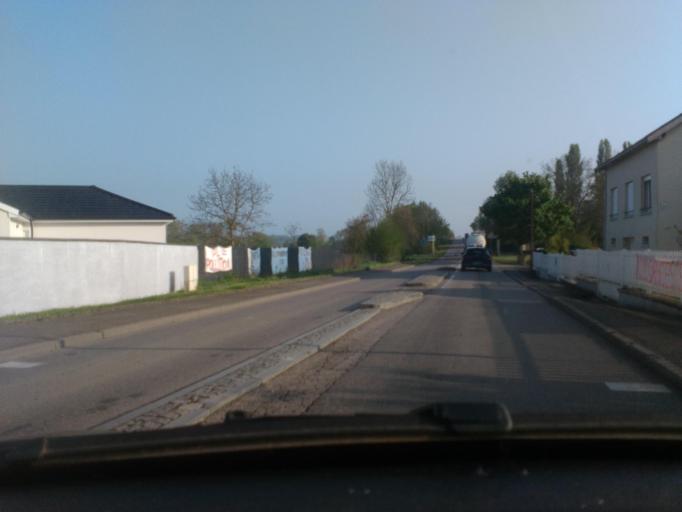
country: FR
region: Lorraine
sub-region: Departement de Meurthe-et-Moselle
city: Art-sur-Meurthe
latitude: 48.6162
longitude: 6.2542
